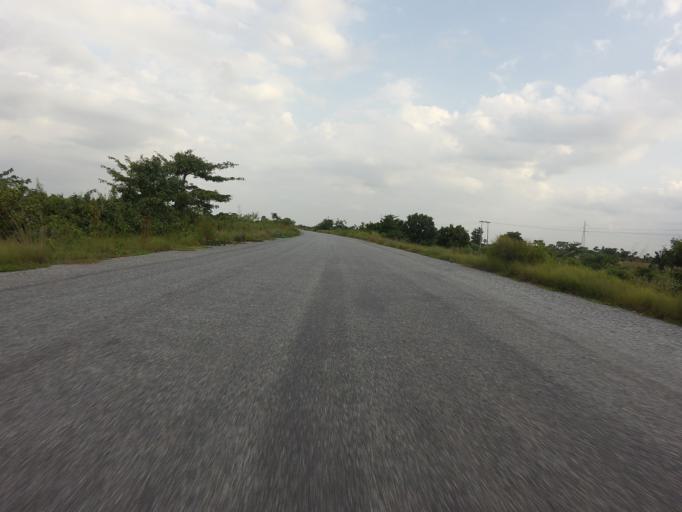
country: GH
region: Volta
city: Ho
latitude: 6.3853
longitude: 0.5289
